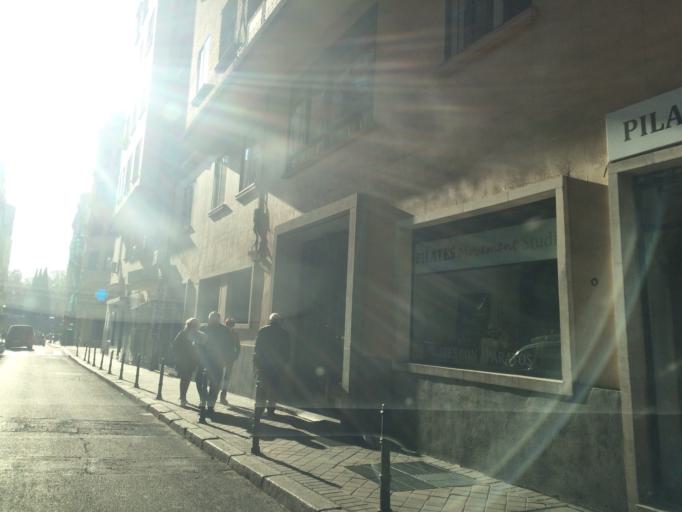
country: ES
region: Madrid
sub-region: Provincia de Madrid
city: Chamberi
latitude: 40.4259
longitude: -3.7150
